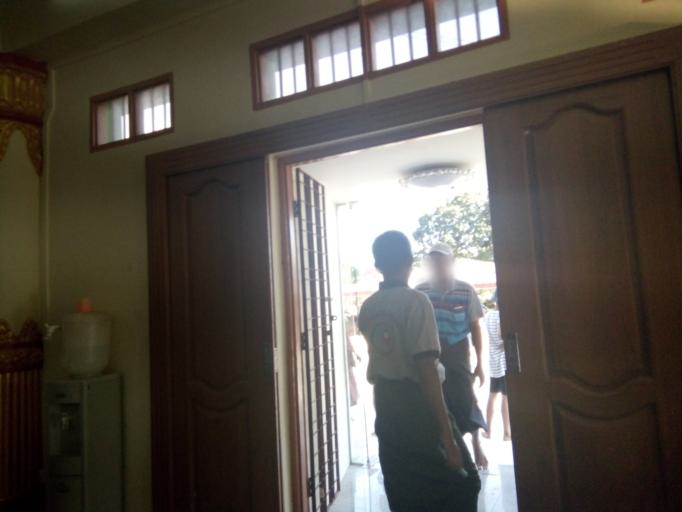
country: MM
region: Bago
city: Thanatpin
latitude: 17.2739
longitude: 96.2353
